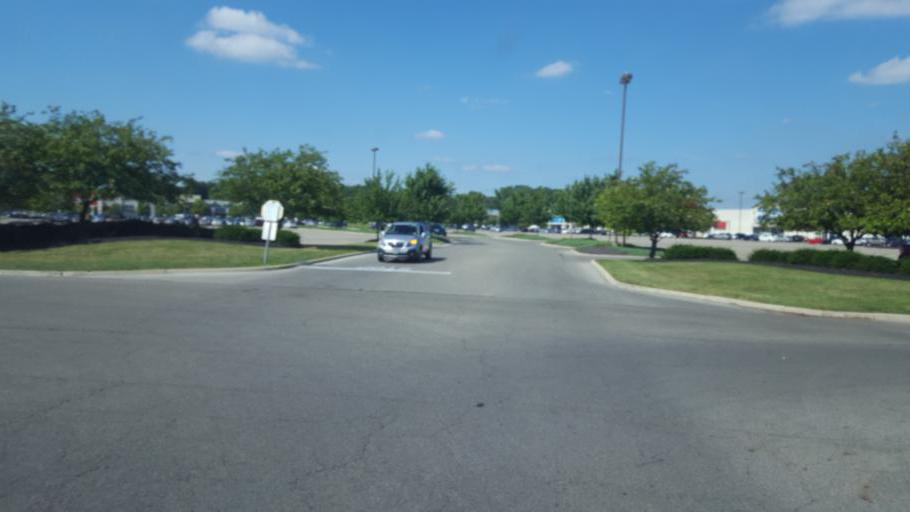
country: US
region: Ohio
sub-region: Franklin County
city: Dublin
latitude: 40.0954
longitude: -83.0871
